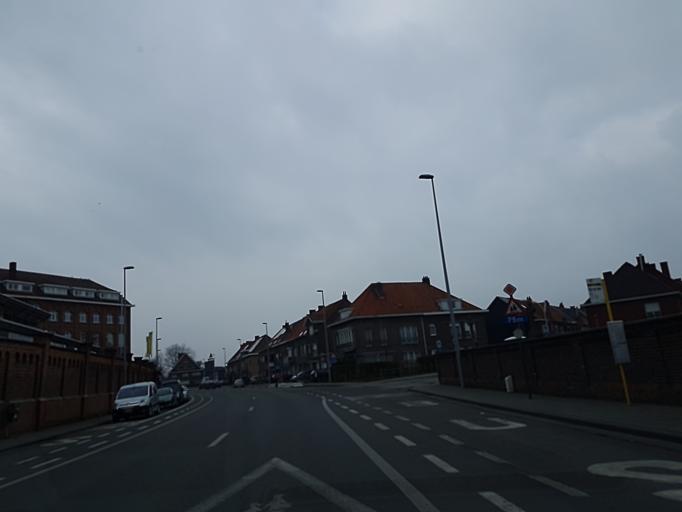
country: BE
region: Flanders
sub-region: Provincie Oost-Vlaanderen
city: Deinze
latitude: 50.9877
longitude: 3.5276
